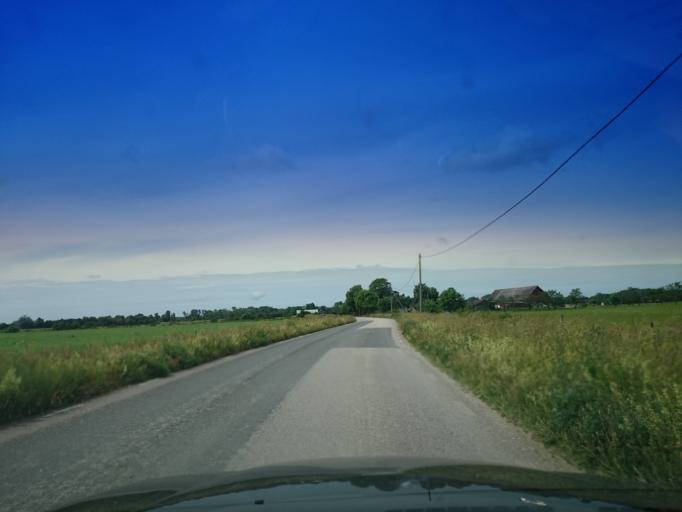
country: SE
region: Gotland
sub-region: Gotland
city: Hemse
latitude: 57.2474
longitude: 18.5346
